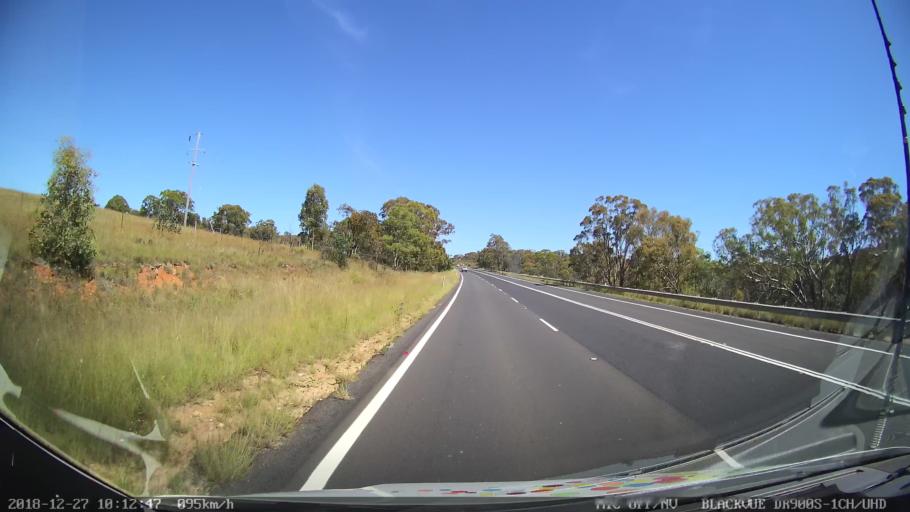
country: AU
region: New South Wales
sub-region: Bathurst Regional
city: Kelso
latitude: -33.4395
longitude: 149.7563
